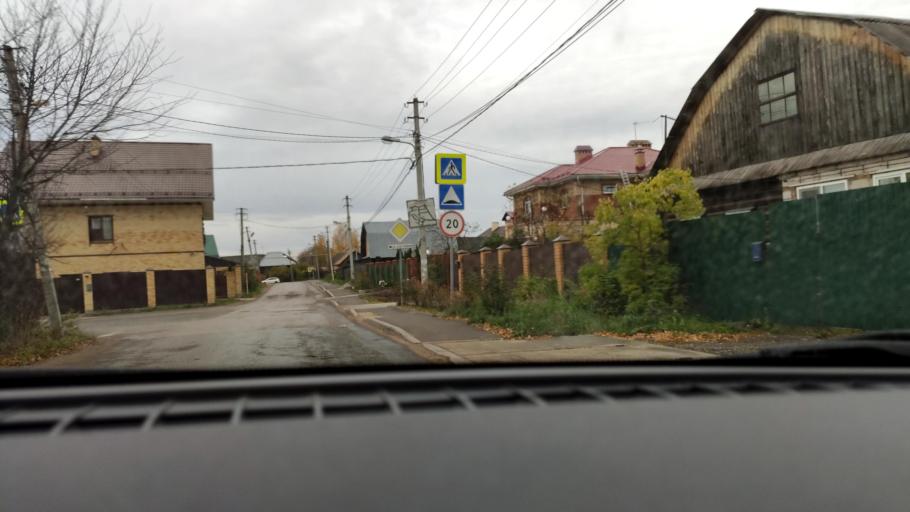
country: RU
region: Perm
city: Froly
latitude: 57.9512
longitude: 56.2998
